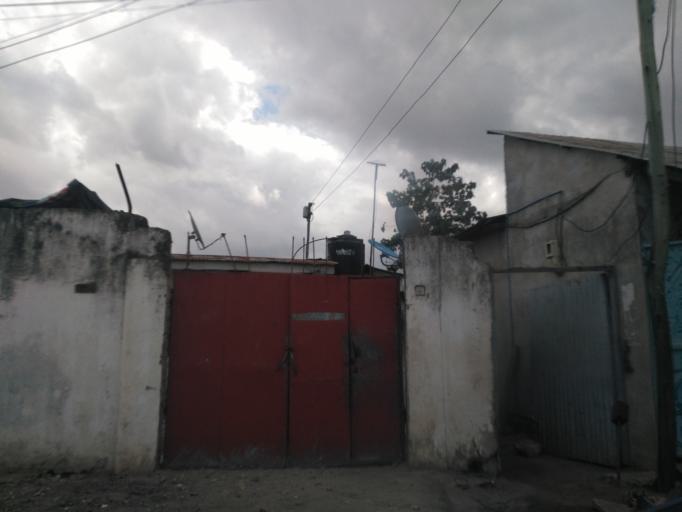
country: TZ
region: Dar es Salaam
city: Magomeni
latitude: -6.7968
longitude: 39.2672
